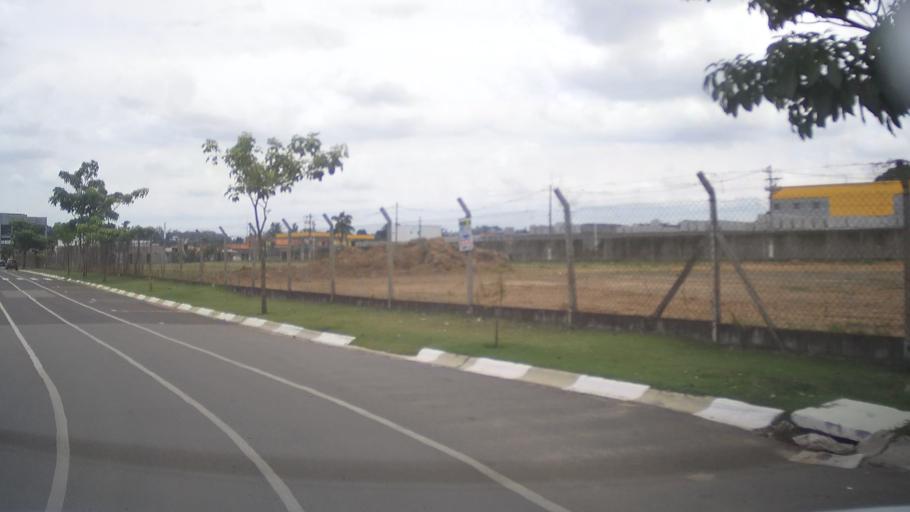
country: BR
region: Sao Paulo
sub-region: Itupeva
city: Itupeva
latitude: -23.1532
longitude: -47.0502
